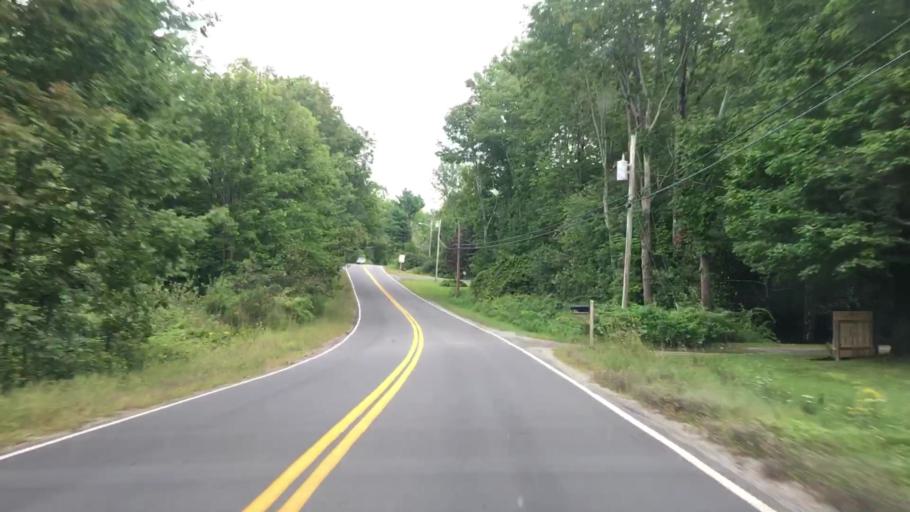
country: US
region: Maine
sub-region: Kennebec County
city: Hallowell
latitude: 44.2647
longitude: -69.8027
